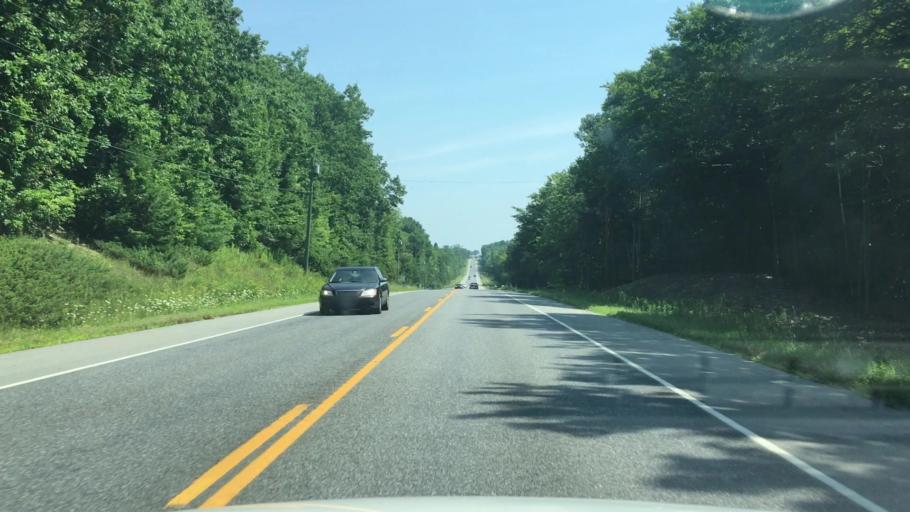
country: US
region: Maine
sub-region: Kennebec County
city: Monmouth
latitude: 44.2605
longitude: -70.0493
